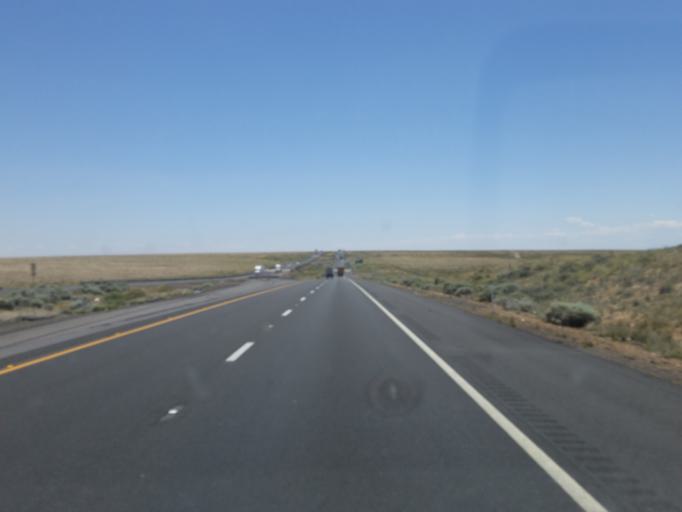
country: US
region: Arizona
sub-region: Coconino County
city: LeChee
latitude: 35.1329
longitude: -111.1946
